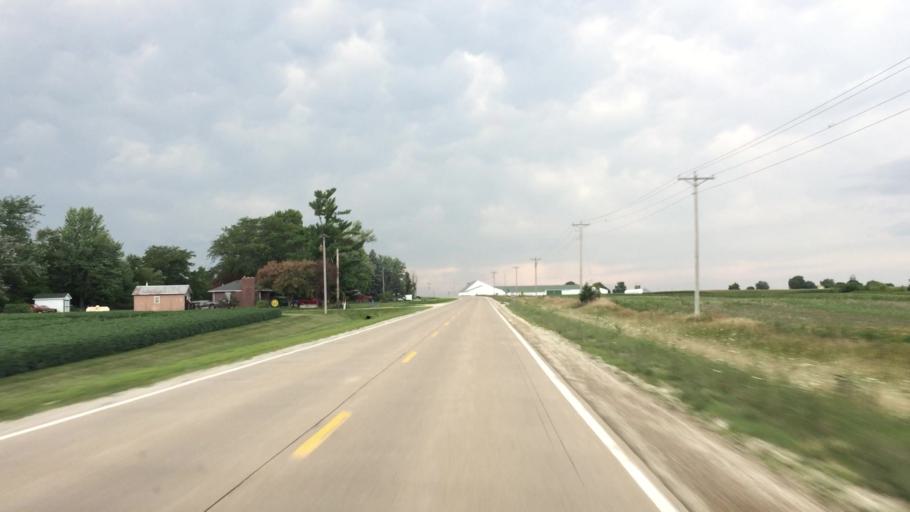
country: US
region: Iowa
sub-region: Lee County
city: Fort Madison
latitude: 40.7333
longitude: -91.3292
